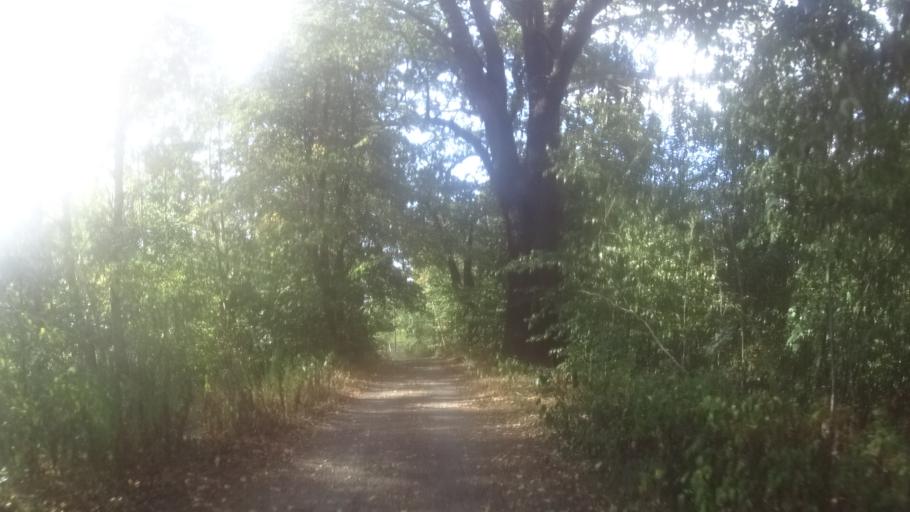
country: CZ
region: Kralovehradecky
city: Trebechovice pod Orebem
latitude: 50.1894
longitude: 16.0075
